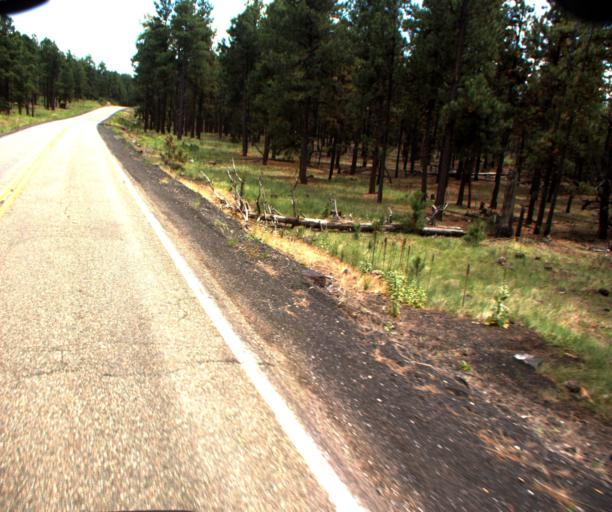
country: US
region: Arizona
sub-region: Coconino County
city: Flagstaff
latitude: 35.3056
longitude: -111.7704
